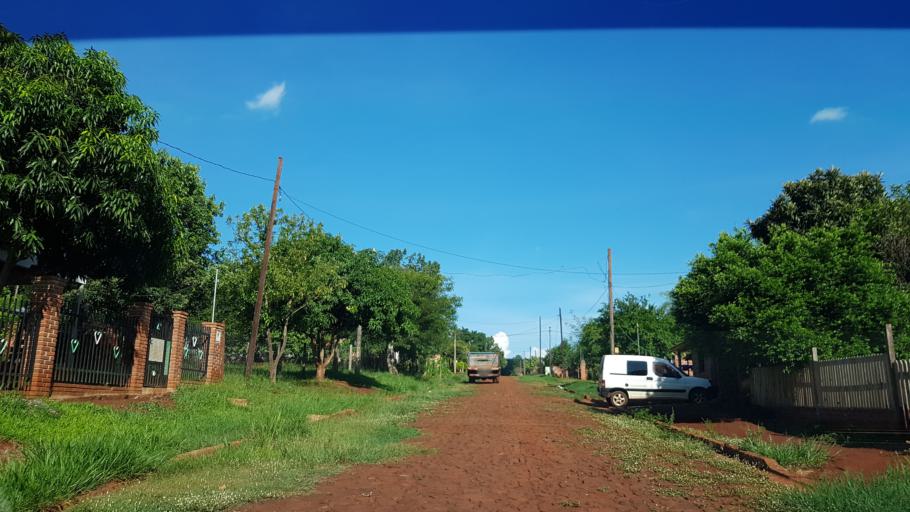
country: AR
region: Misiones
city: Puerto Libertad
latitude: -25.9127
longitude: -54.5846
